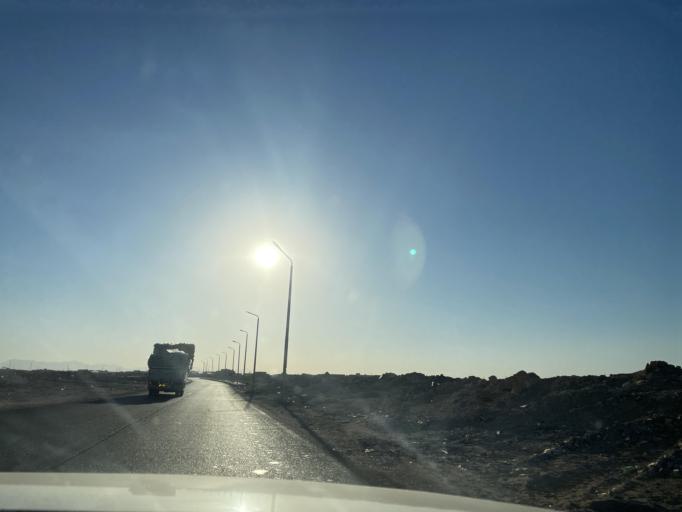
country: EG
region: Red Sea
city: Hurghada
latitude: 27.2185
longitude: 33.7909
